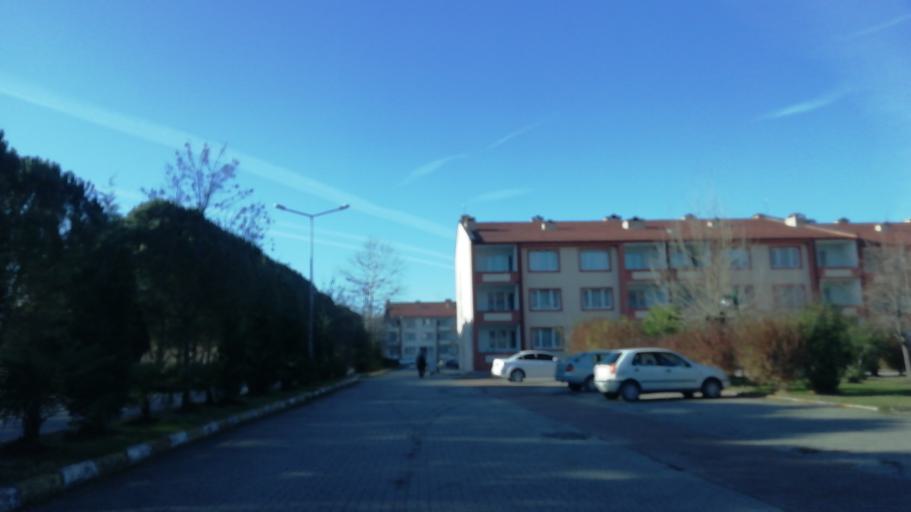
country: TR
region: Sakarya
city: Akyazi
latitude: 40.6263
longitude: 30.6510
